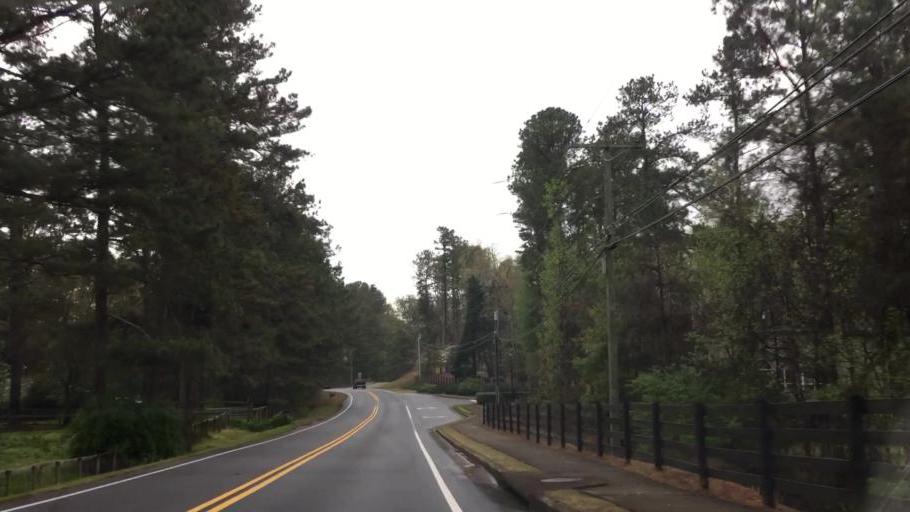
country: US
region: Georgia
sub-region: Fulton County
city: Milton
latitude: 34.1688
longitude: -84.2936
